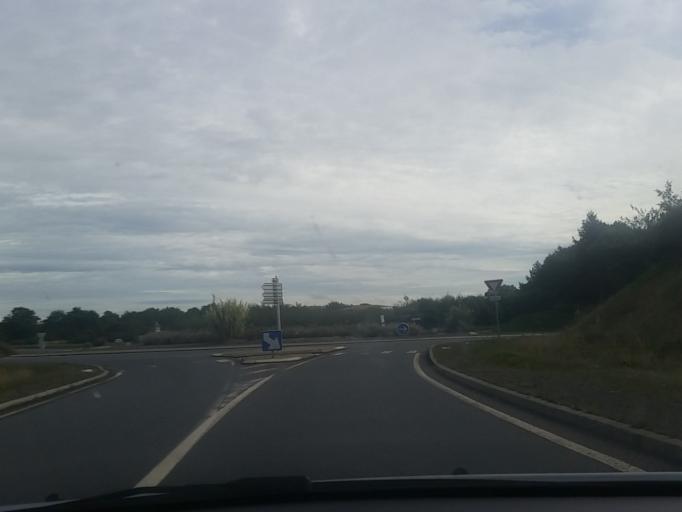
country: FR
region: Pays de la Loire
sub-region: Departement de la Loire-Atlantique
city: Chateaubriant
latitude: 47.7004
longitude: -1.3671
